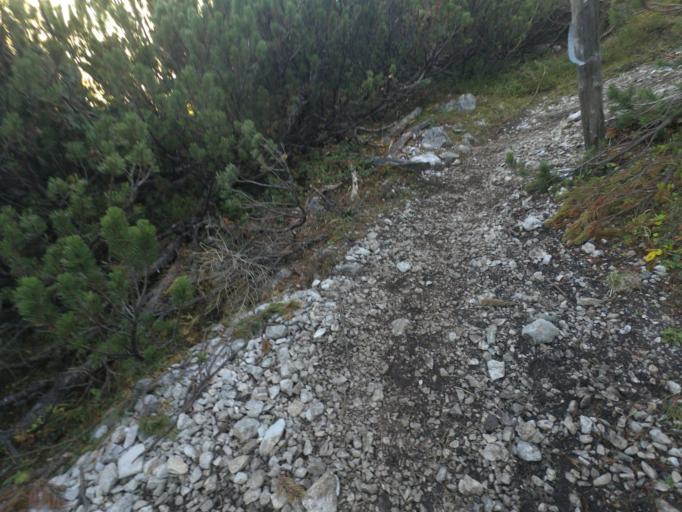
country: AT
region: Salzburg
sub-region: Politischer Bezirk Sankt Johann im Pongau
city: Werfenweng
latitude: 47.4887
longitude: 13.2321
